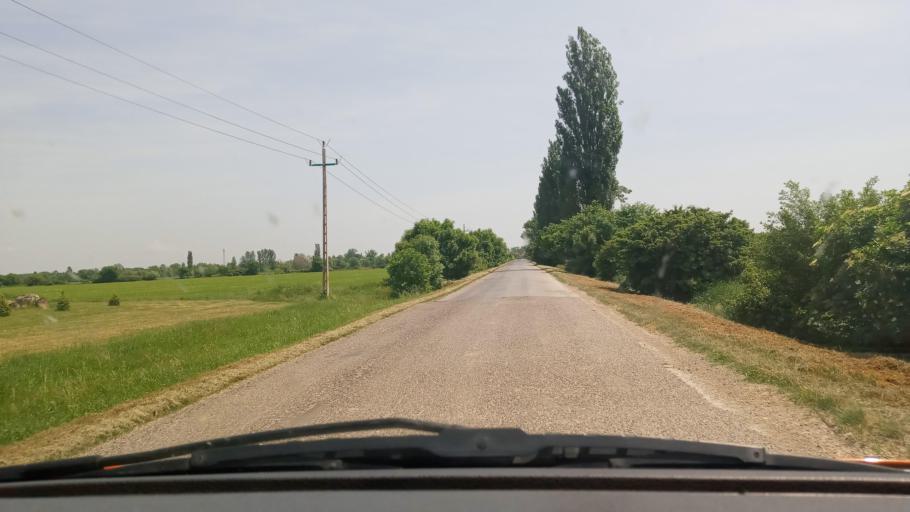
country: HU
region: Baranya
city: Szigetvar
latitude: 45.9656
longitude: 17.7011
